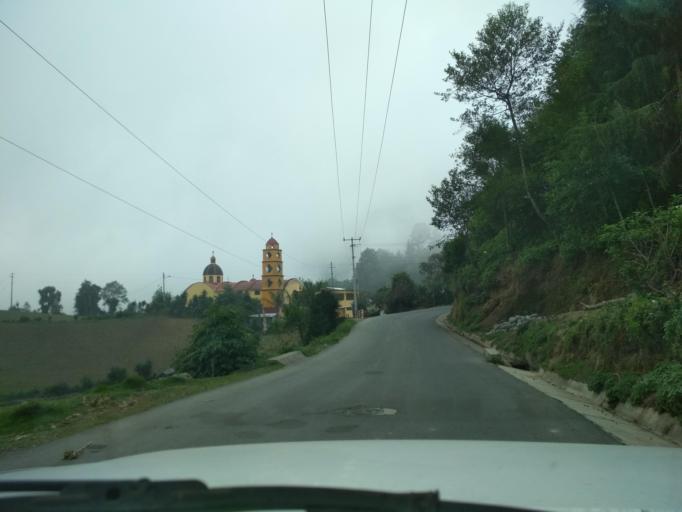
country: MX
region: Veracruz
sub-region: Mariano Escobedo
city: San Isidro el Berro
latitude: 18.9458
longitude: -97.1997
